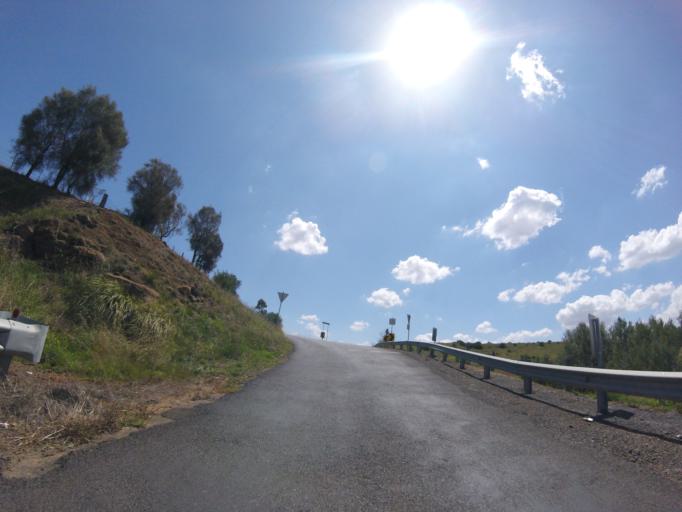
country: AU
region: Victoria
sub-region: Hume
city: Sunbury
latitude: -37.5841
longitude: 144.7682
